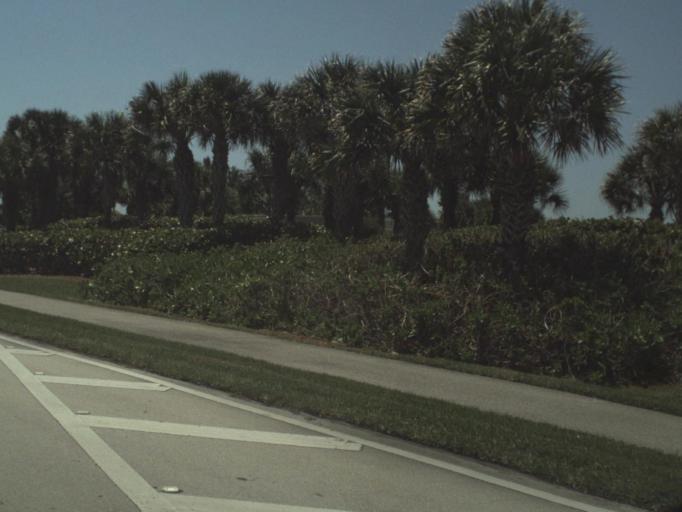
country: US
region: Florida
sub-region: Brevard County
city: Micco
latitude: 27.9243
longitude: -80.4841
